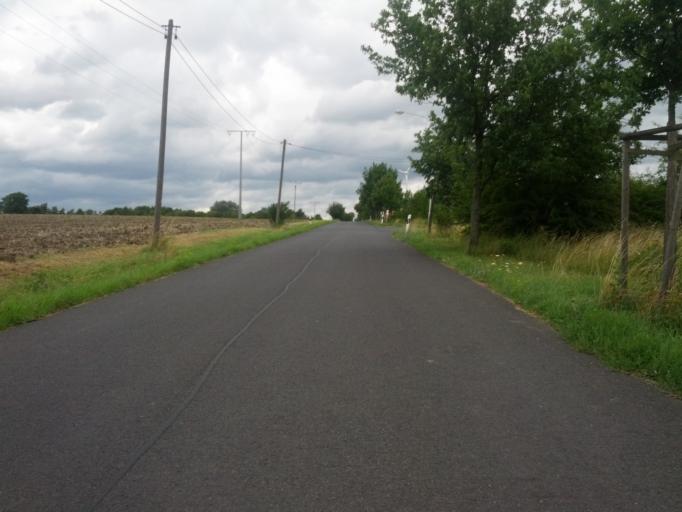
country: DE
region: Thuringia
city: Bischofroda
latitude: 50.9931
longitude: 10.3737
